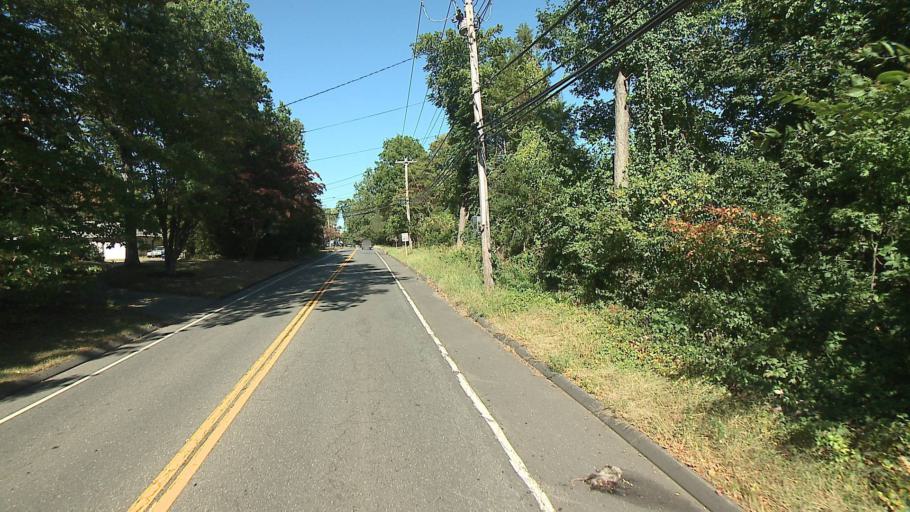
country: US
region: Connecticut
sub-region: New Haven County
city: Orange
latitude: 41.2959
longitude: -73.0416
